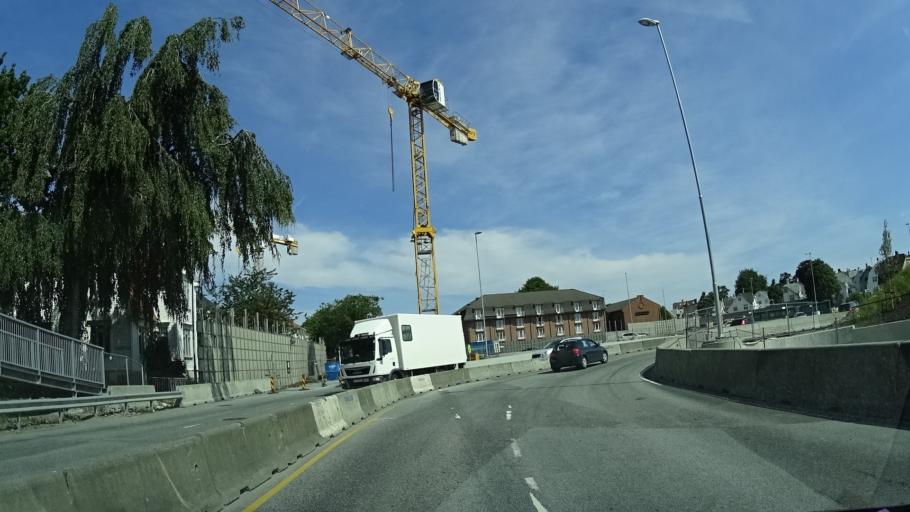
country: NO
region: Rogaland
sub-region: Stavanger
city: Stavanger
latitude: 58.9625
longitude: 5.7227
